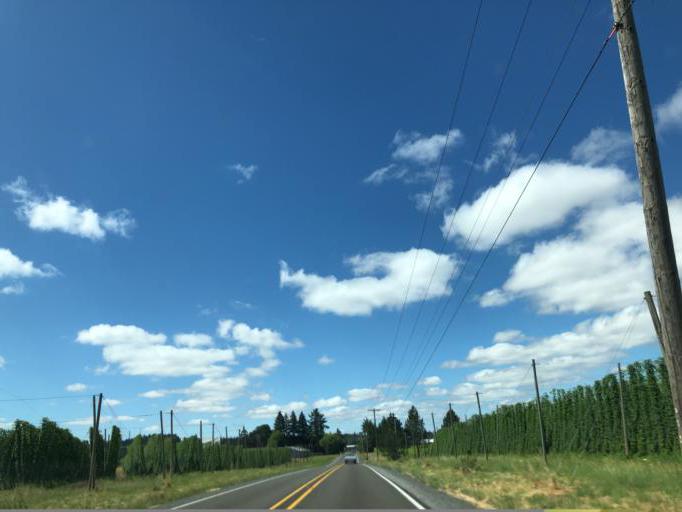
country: US
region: Oregon
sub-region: Marion County
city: Silverton
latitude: 45.0262
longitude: -122.7656
